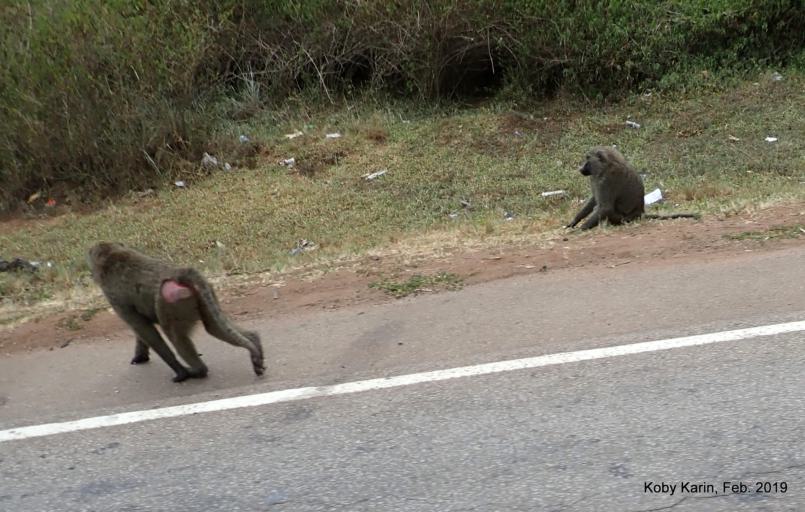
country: UG
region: Eastern Region
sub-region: Busia District
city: Busia
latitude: 0.4987
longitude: 33.9941
